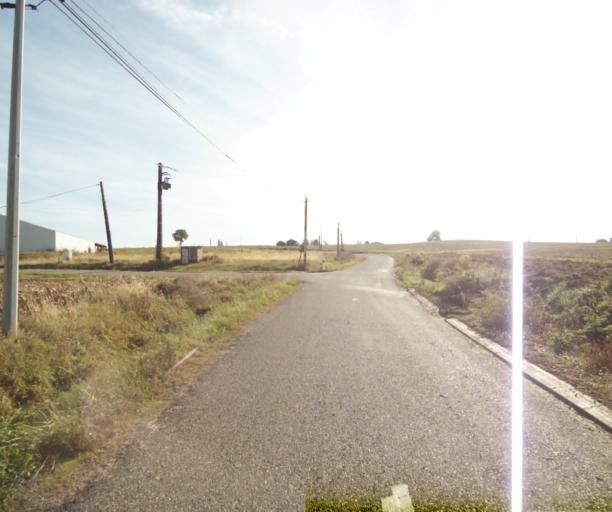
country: FR
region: Midi-Pyrenees
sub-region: Departement du Tarn-et-Garonne
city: Nohic
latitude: 43.9019
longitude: 1.4722
